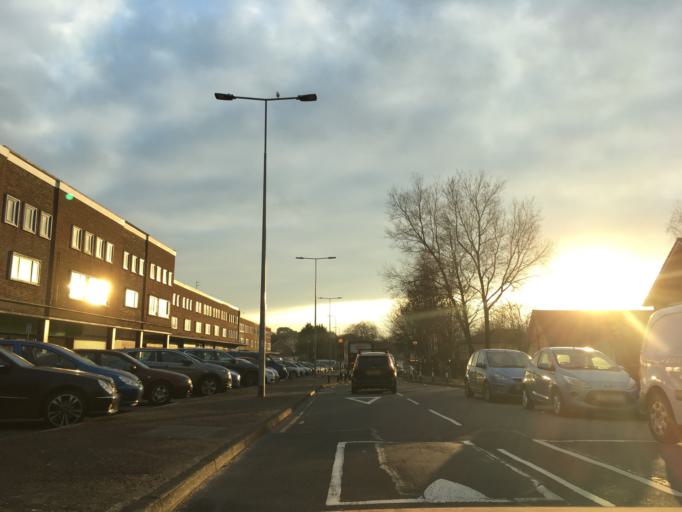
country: GB
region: Wales
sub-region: Newport
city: Marshfield
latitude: 51.5209
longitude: -3.1201
